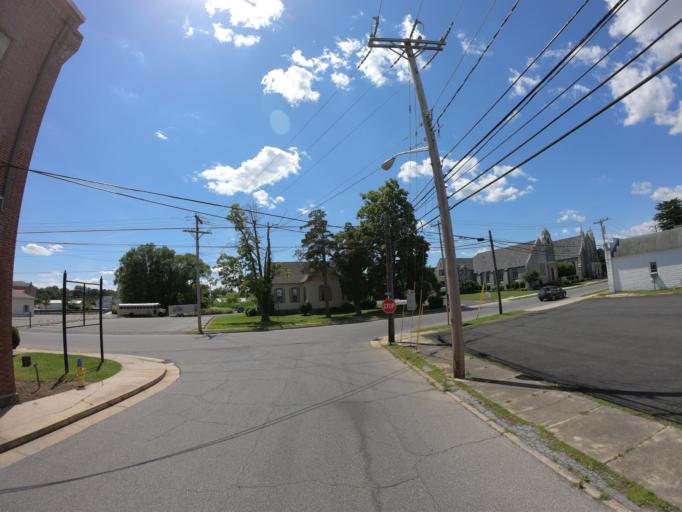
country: US
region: Delaware
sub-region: Sussex County
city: Milford
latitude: 38.9130
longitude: -75.4300
